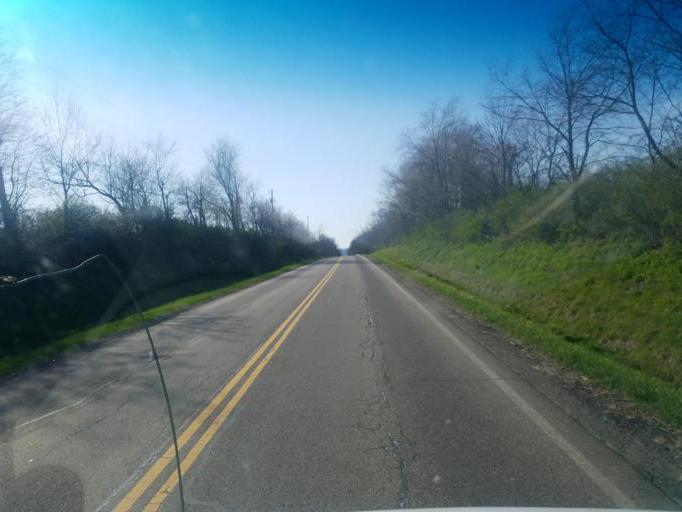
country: US
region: Ohio
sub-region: Knox County
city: Oak Hill
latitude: 40.3408
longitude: -82.1935
